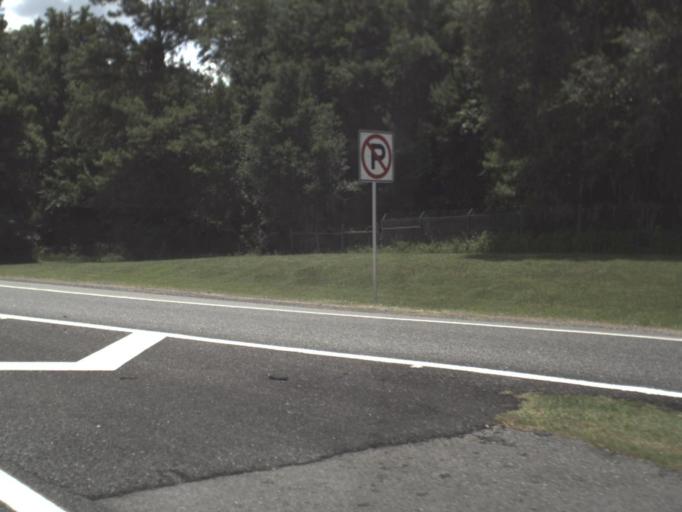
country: US
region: Florida
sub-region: Alachua County
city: High Springs
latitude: 29.9769
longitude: -82.5782
